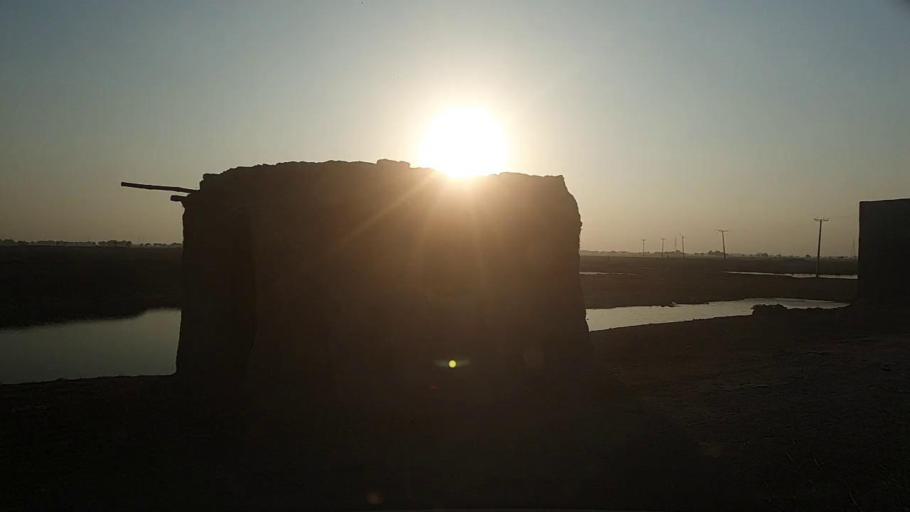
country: PK
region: Sindh
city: Mehar
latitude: 27.1980
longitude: 67.7575
